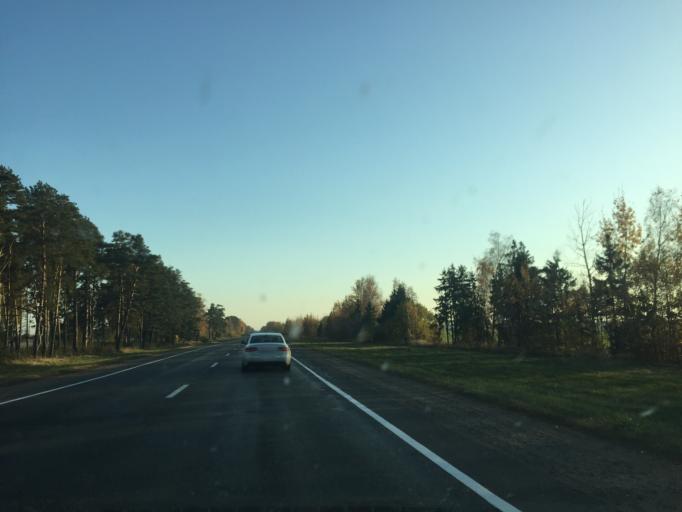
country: BY
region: Mogilev
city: Poselok Voskhod
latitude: 53.7445
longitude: 30.3659
